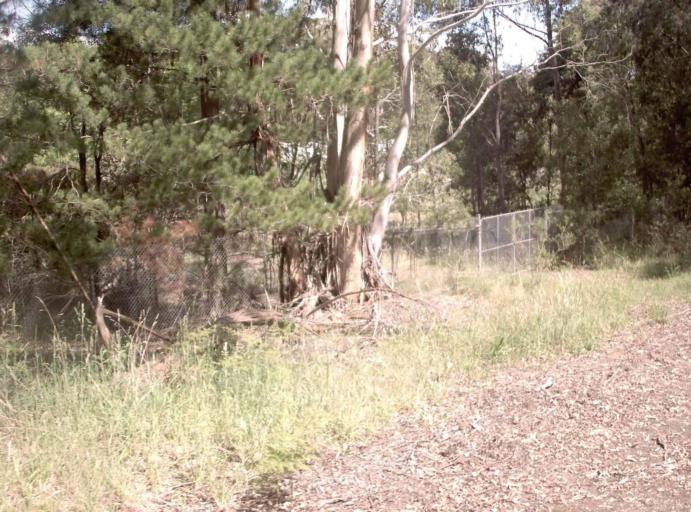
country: AU
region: New South Wales
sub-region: Bombala
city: Bombala
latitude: -37.1869
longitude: 148.7256
